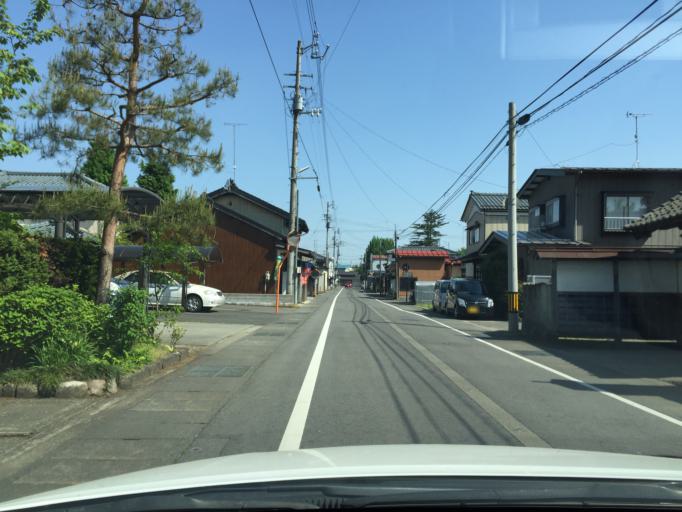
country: JP
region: Niigata
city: Muramatsu
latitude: 37.6884
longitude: 139.1765
